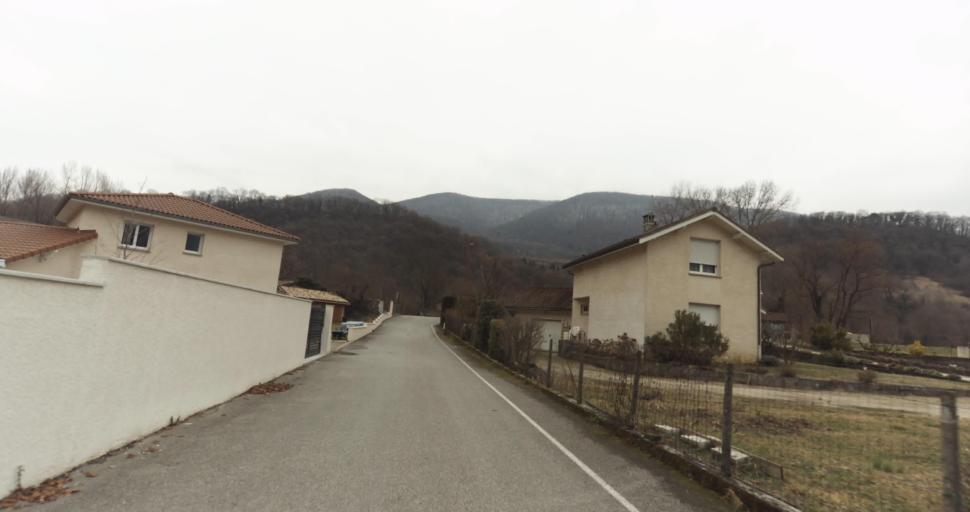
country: FR
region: Rhone-Alpes
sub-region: Departement de l'Isere
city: Vif
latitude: 45.0329
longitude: 5.6551
